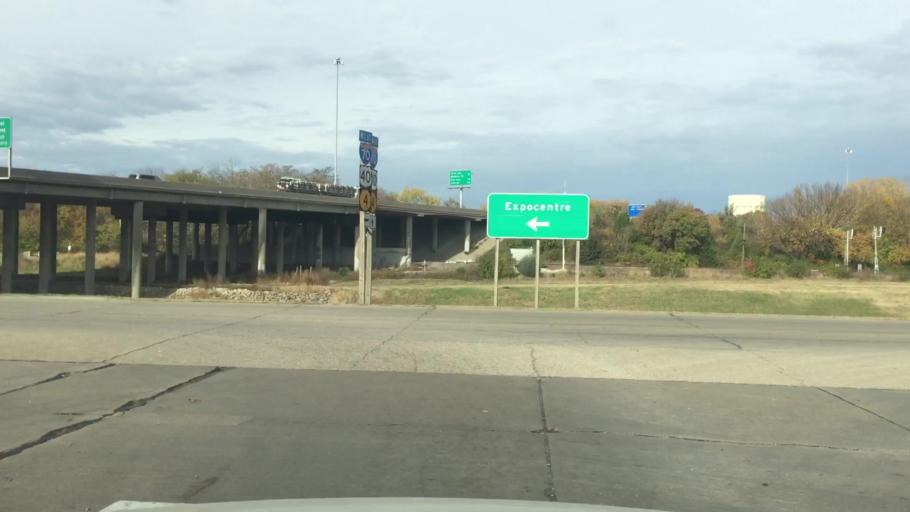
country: US
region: Kansas
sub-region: Shawnee County
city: Topeka
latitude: 39.0403
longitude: -95.6676
